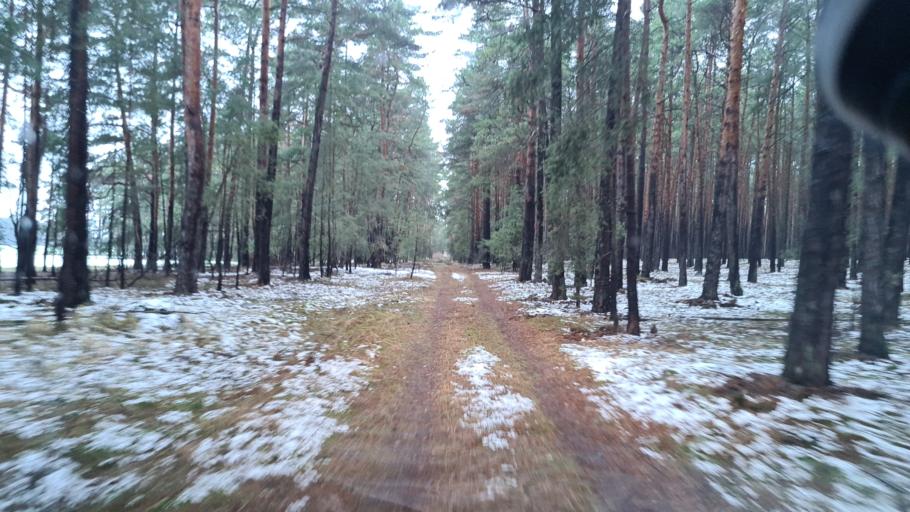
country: DE
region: Brandenburg
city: Schenkendobern
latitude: 51.8981
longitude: 14.5884
